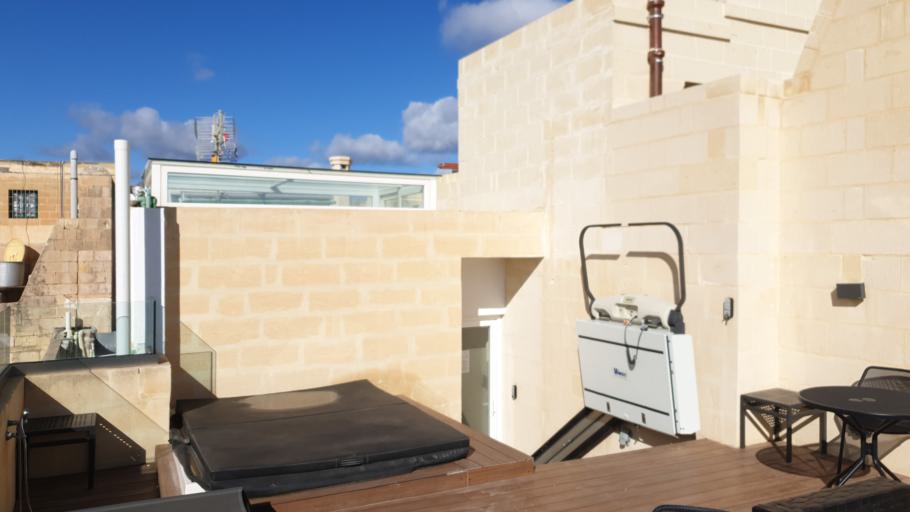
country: MT
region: Il-Belt Valletta
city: Valletta
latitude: 35.8974
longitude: 14.5141
